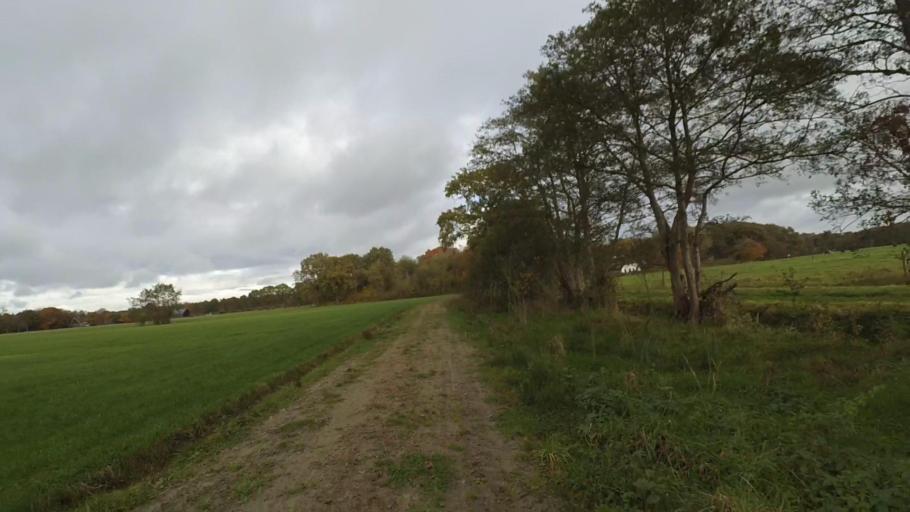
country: NL
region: Gelderland
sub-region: Gemeente Barneveld
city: Terschuur
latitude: 52.1407
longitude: 5.5190
